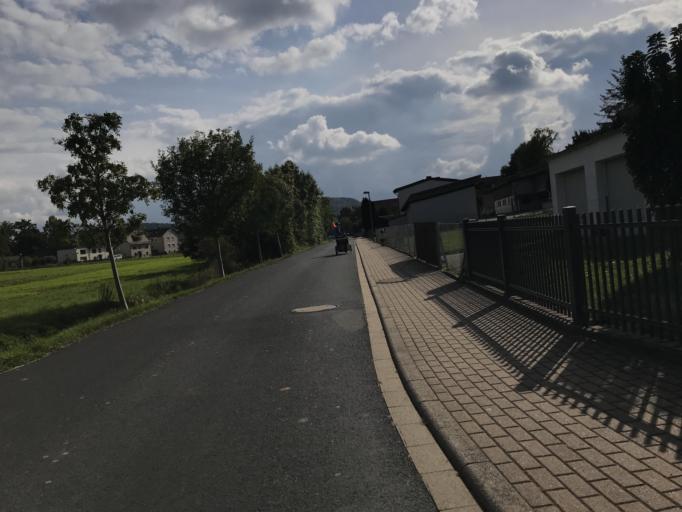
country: DE
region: Hesse
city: Felsberg
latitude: 51.1378
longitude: 9.4237
